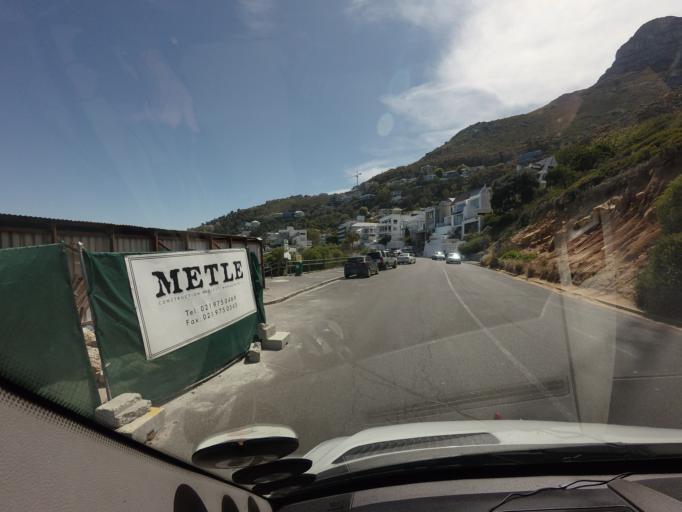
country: ZA
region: Western Cape
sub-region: City of Cape Town
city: Cape Town
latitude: -33.9363
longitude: 18.3785
